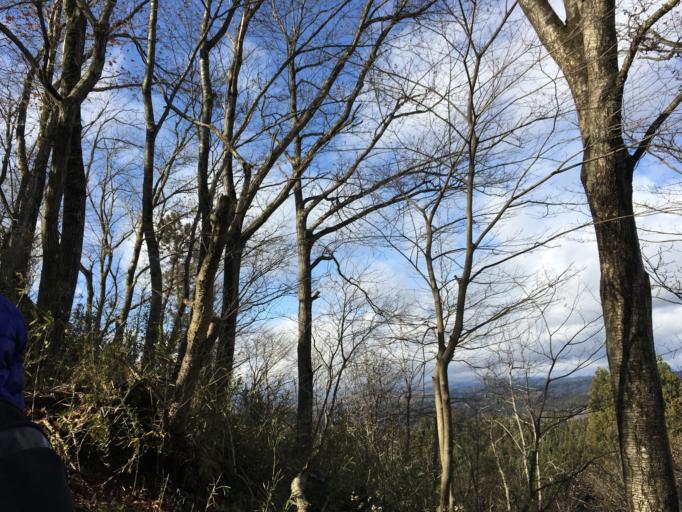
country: JP
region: Iwate
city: Ichinoseki
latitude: 38.9925
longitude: 141.0982
